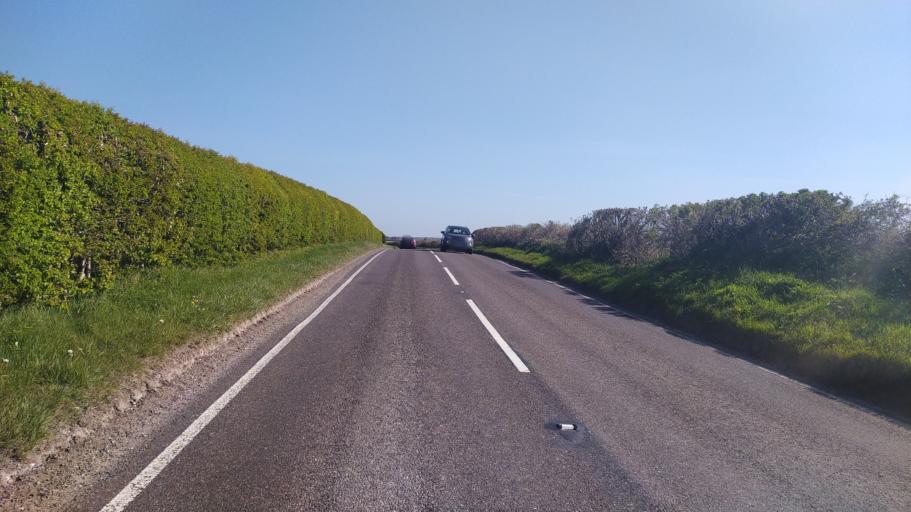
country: GB
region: England
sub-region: Dorset
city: Wimborne Minster
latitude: 50.8693
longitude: -1.9839
